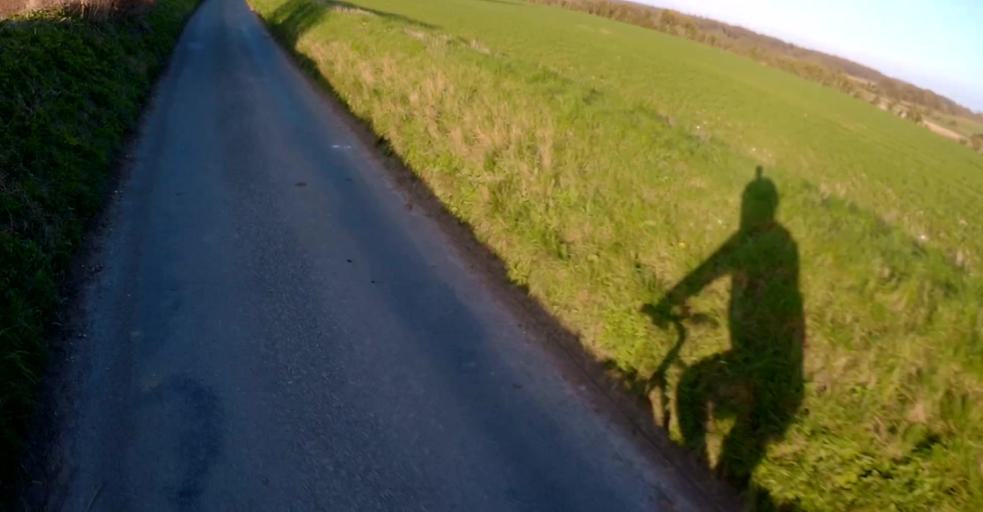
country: GB
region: England
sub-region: Hampshire
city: Basingstoke
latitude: 51.2314
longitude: -1.0914
